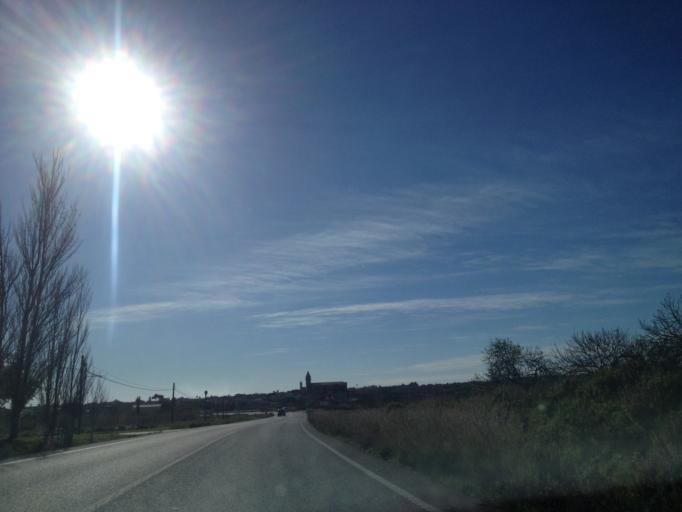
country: ES
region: Balearic Islands
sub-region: Illes Balears
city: Petra
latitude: 39.6240
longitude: 3.1096
